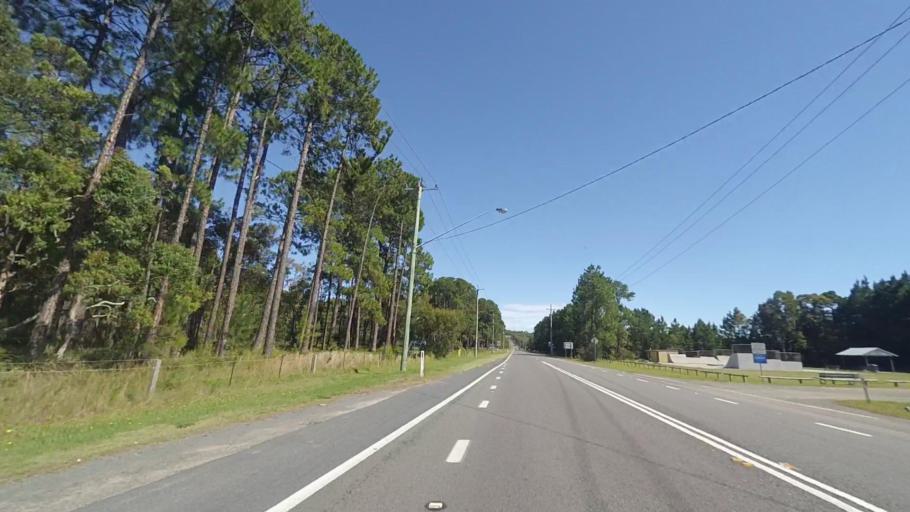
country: AU
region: New South Wales
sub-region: Great Lakes
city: Hawks Nest
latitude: -32.6506
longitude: 152.1486
